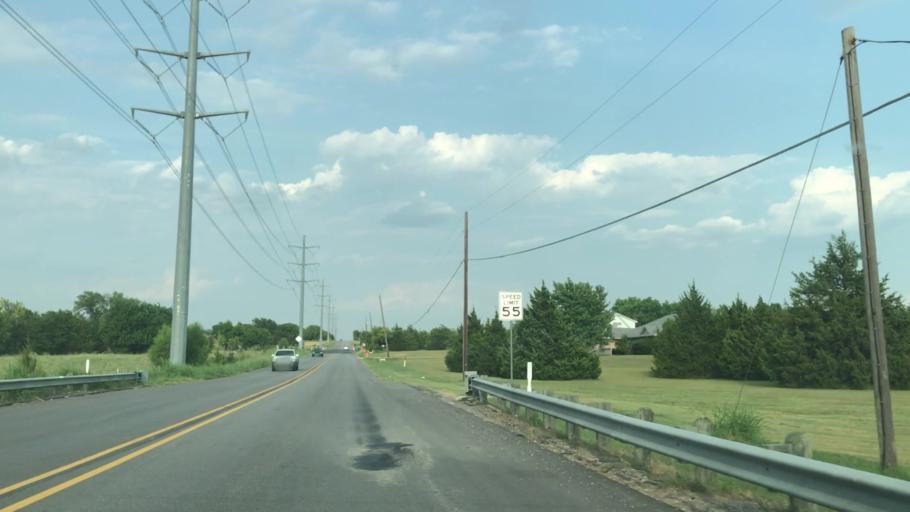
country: US
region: Texas
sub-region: Rockwall County
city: Fate
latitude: 32.9362
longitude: -96.4120
